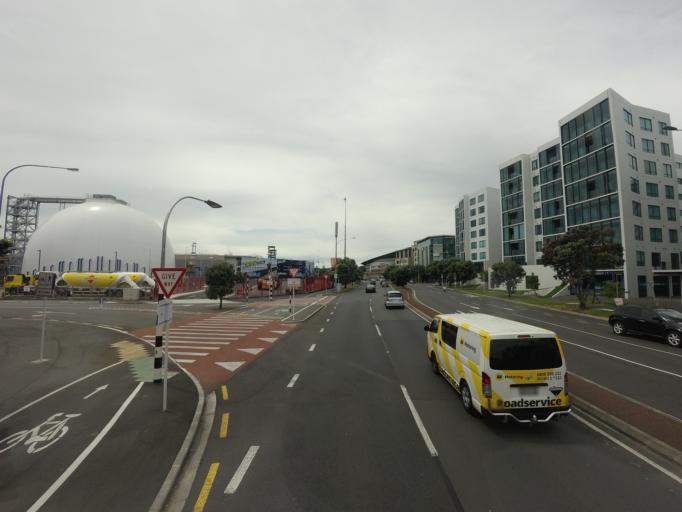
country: NZ
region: Auckland
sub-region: Auckland
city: Auckland
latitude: -36.8452
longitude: 174.7743
